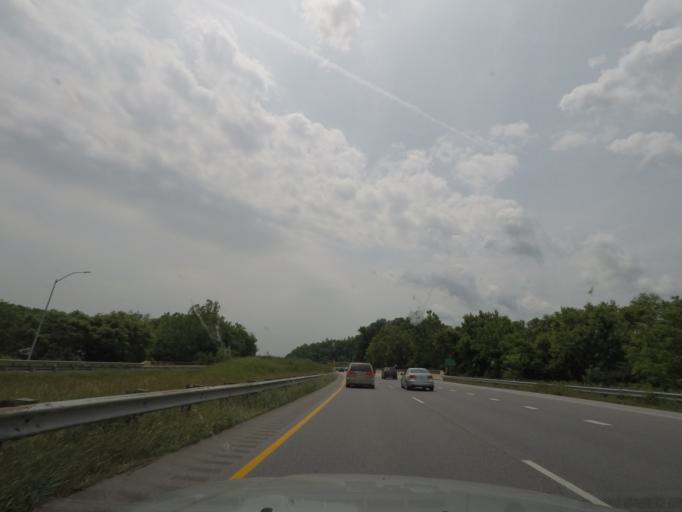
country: US
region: Maryland
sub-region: Frederick County
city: Thurmont
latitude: 39.6259
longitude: -77.4184
